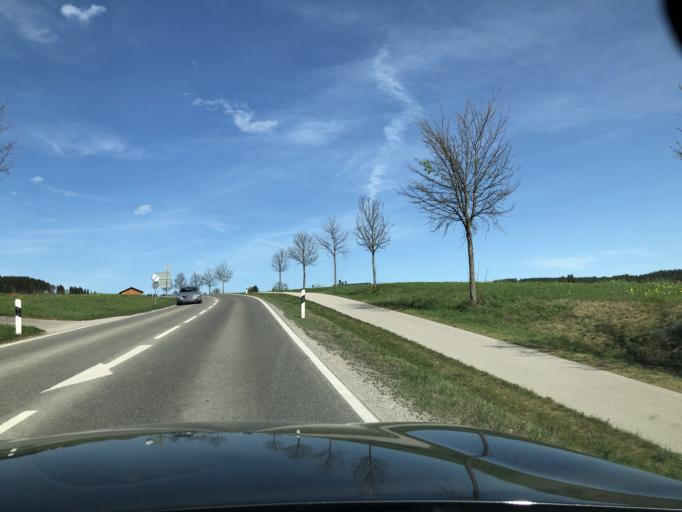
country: DE
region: Bavaria
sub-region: Swabia
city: Eisenberg
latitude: 47.6159
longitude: 10.6140
